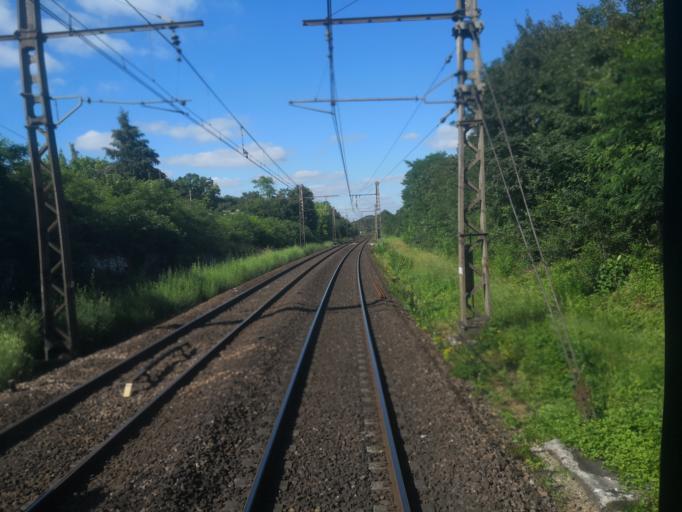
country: FR
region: Ile-de-France
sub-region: Departement de Seine-et-Marne
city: Avon
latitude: 48.4199
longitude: 2.7291
